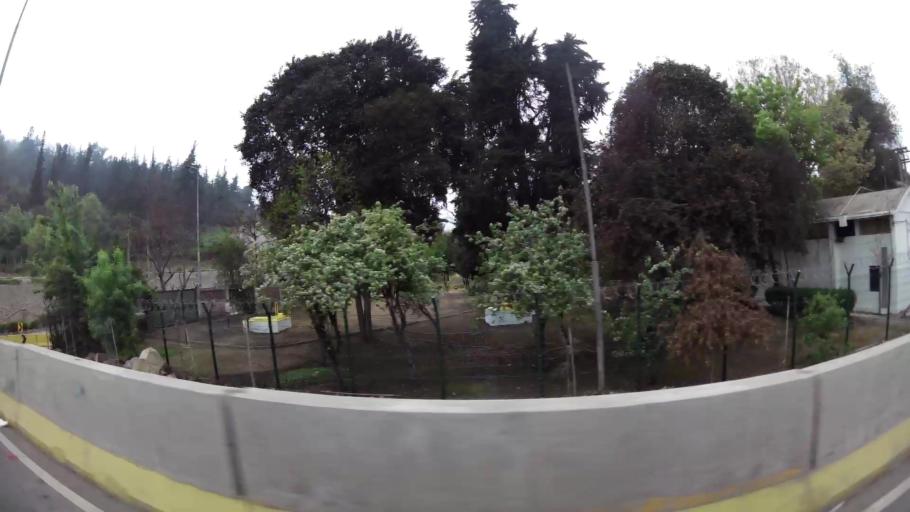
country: CL
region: Santiago Metropolitan
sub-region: Provincia de Santiago
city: Santiago
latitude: -33.4152
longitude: -70.6128
